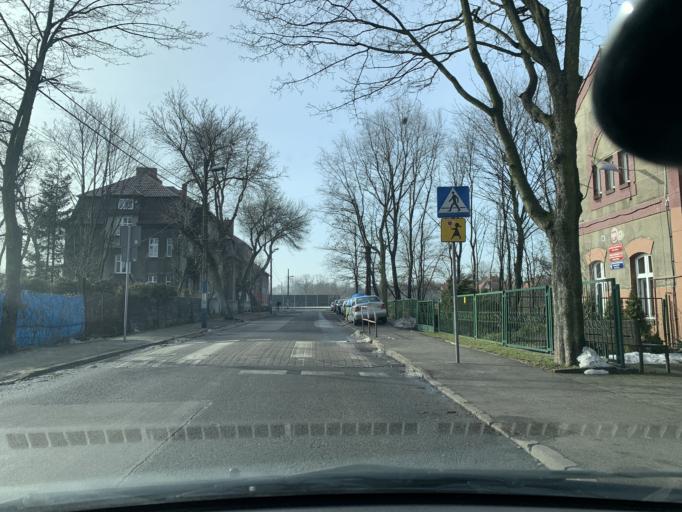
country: PL
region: Silesian Voivodeship
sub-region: Swietochlowice
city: Swietochlowice
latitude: 50.3015
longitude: 18.8798
